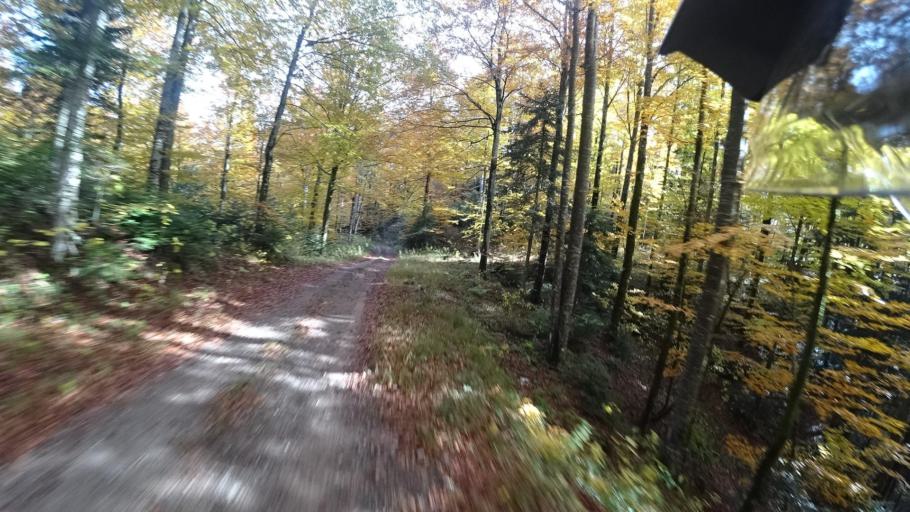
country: HR
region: Karlovacka
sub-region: Grad Ogulin
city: Ogulin
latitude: 45.2104
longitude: 15.0923
